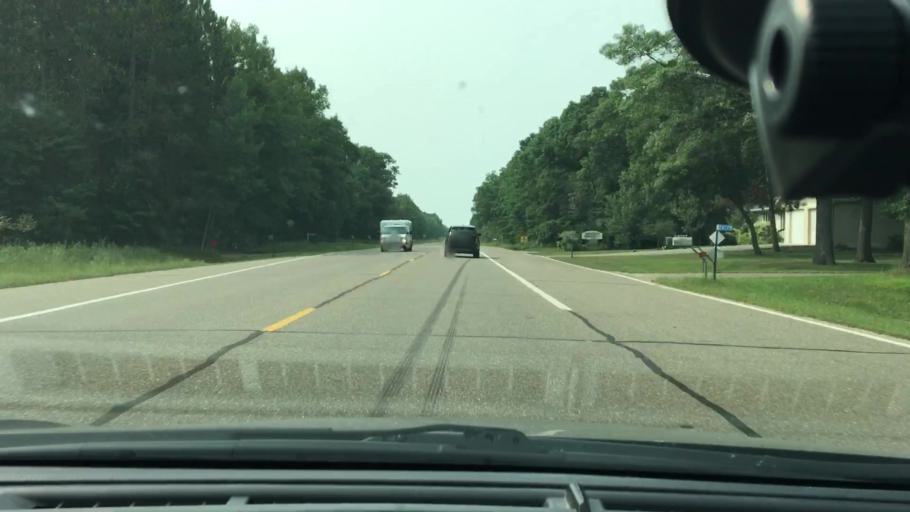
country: US
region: Minnesota
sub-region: Crow Wing County
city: Breezy Point
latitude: 46.5110
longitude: -94.1346
